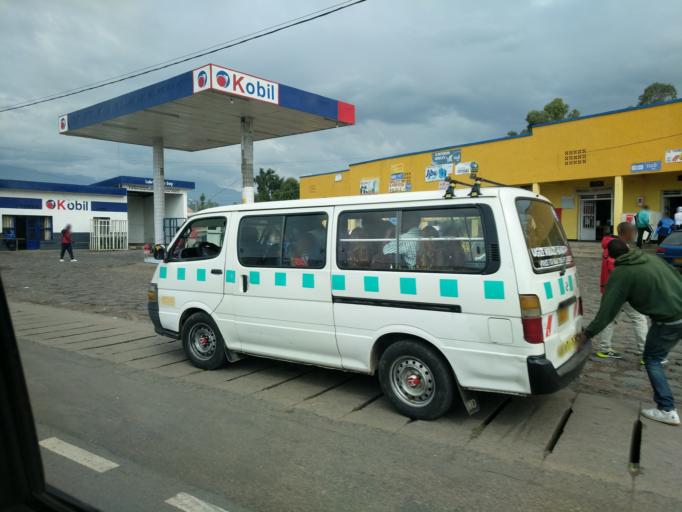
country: RW
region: Northern Province
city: Musanze
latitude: -1.4985
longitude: 29.6270
